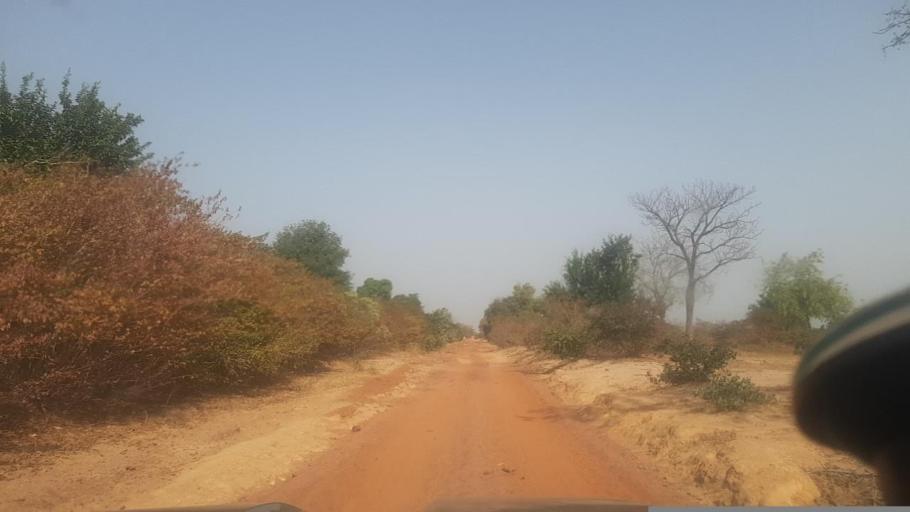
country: ML
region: Segou
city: Bla
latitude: 12.8543
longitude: -5.9783
